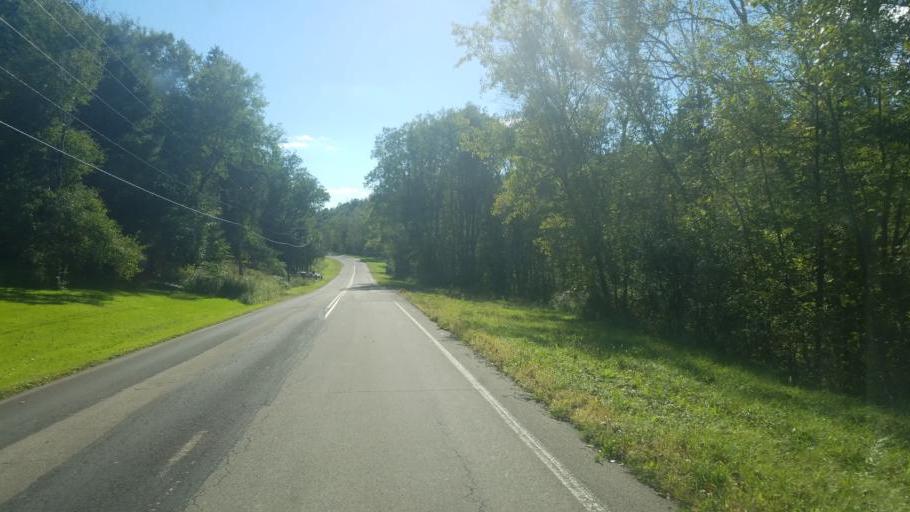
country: US
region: New York
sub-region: Allegany County
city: Friendship
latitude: 42.2985
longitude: -78.1144
